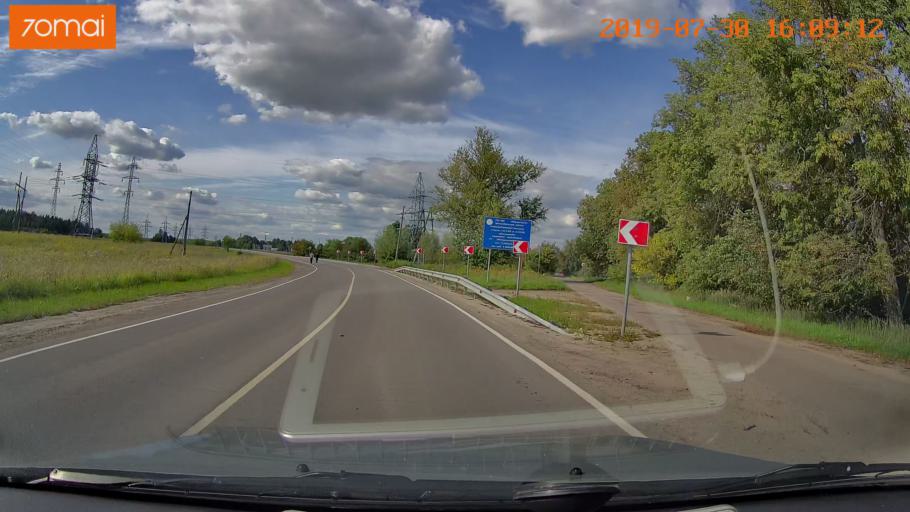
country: RU
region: Moskovskaya
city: Peski
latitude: 55.2515
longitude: 38.7198
